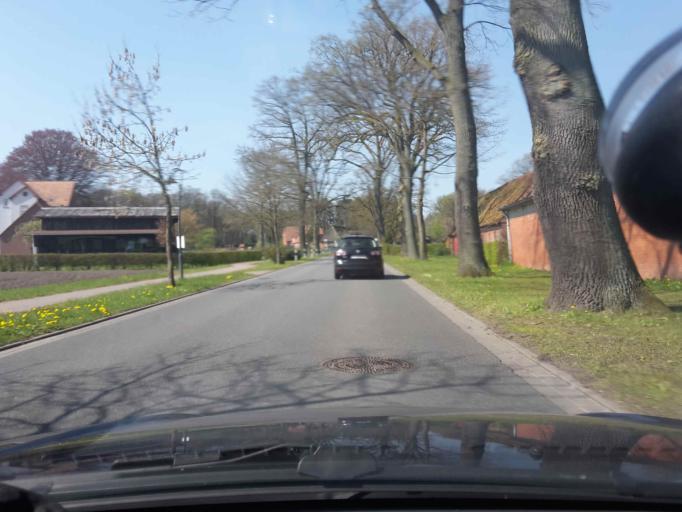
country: DE
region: Lower Saxony
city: Handeloh
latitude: 53.2453
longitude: 9.8356
